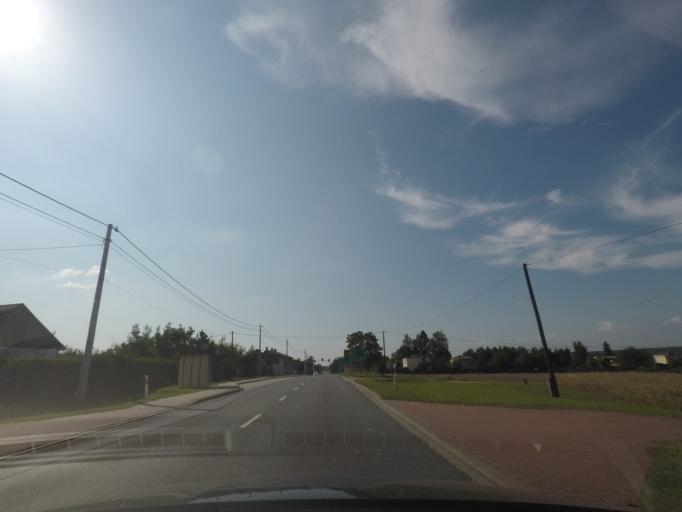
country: PL
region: Silesian Voivodeship
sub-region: Powiat pszczynski
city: Radostowice
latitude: 50.0010
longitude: 18.8839
